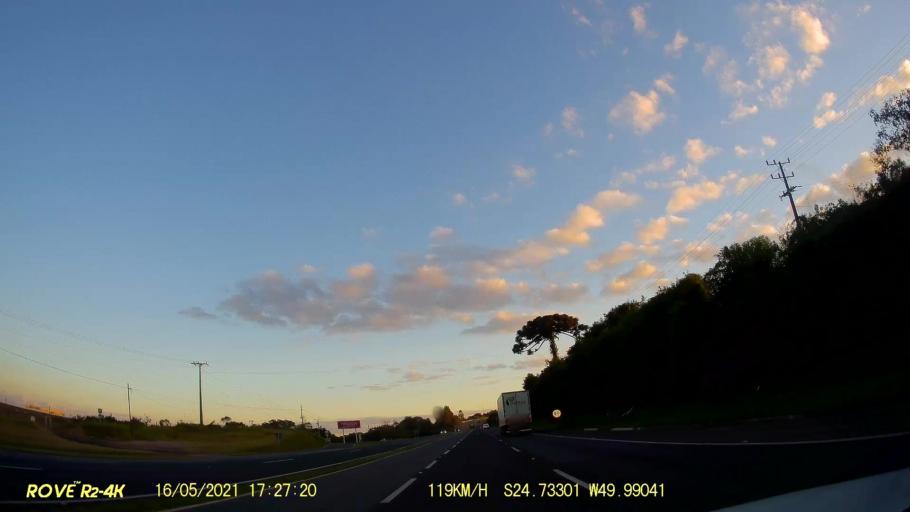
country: BR
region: Parana
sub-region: Castro
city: Castro
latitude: -24.7334
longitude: -49.9906
